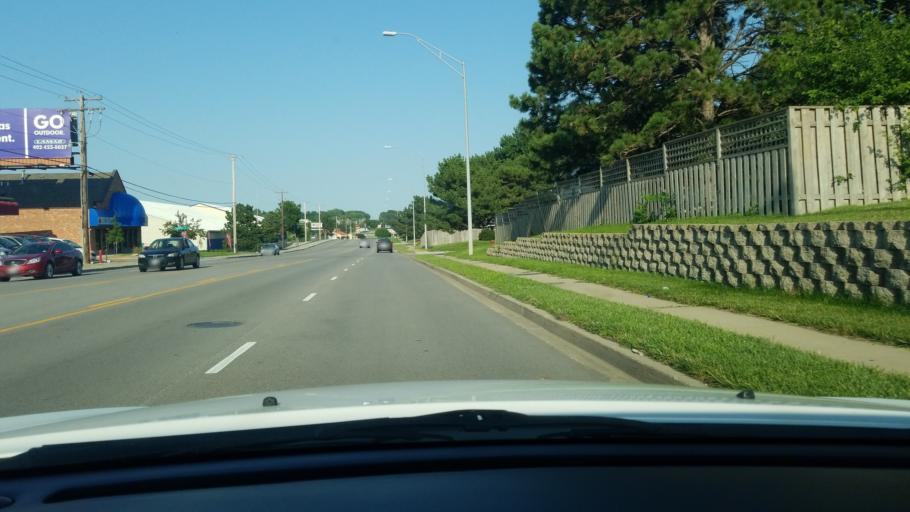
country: US
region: Nebraska
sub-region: Lancaster County
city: Lincoln
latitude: 40.7552
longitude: -96.6504
